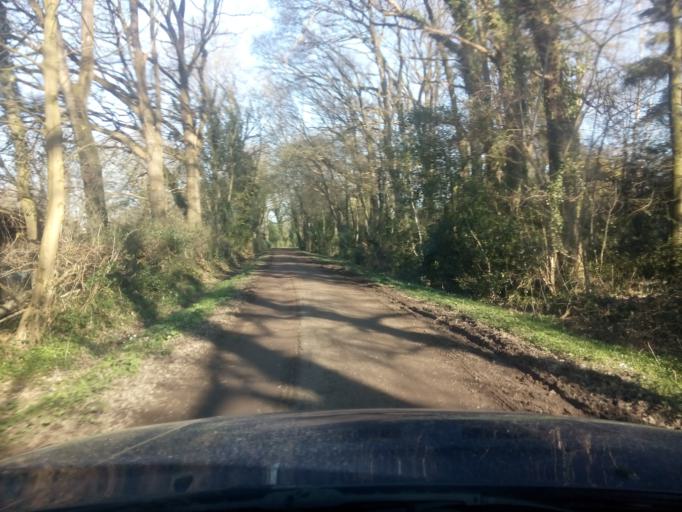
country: DE
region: Lower Saxony
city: Osterholz-Scharmbeck
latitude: 53.2271
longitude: 8.7548
